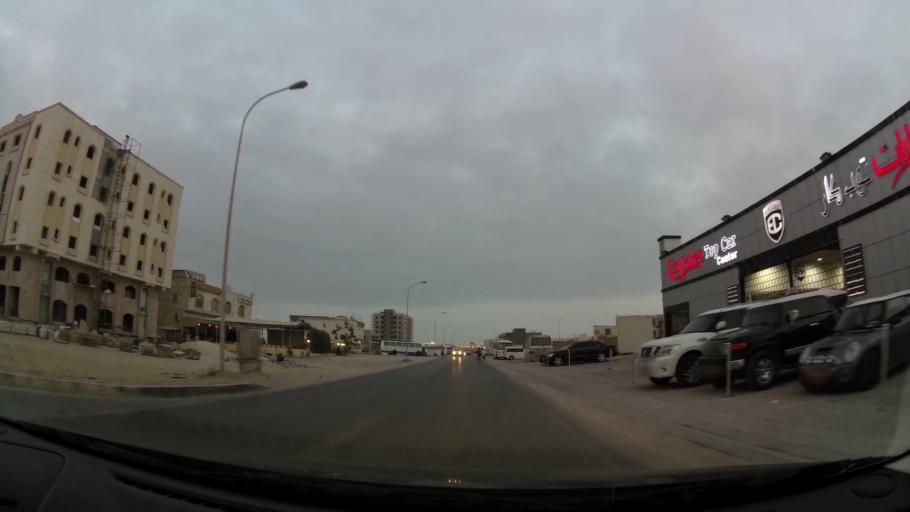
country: OM
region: Zufar
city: Salalah
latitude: 17.0262
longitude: 54.0538
